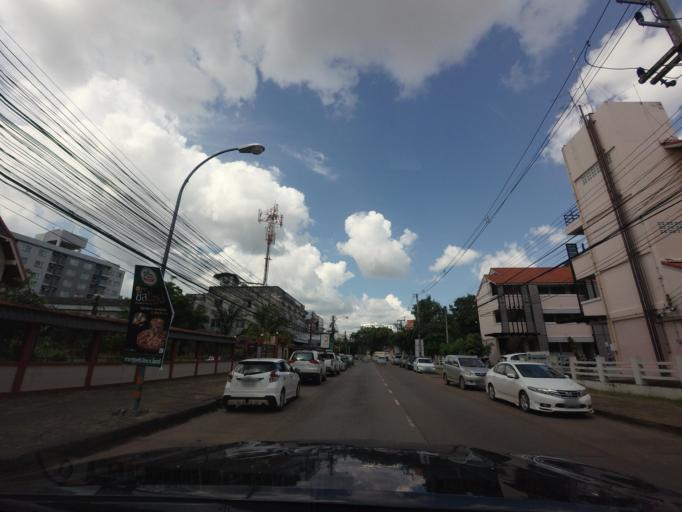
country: TH
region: Changwat Udon Thani
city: Udon Thani
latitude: 17.4126
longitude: 102.7768
